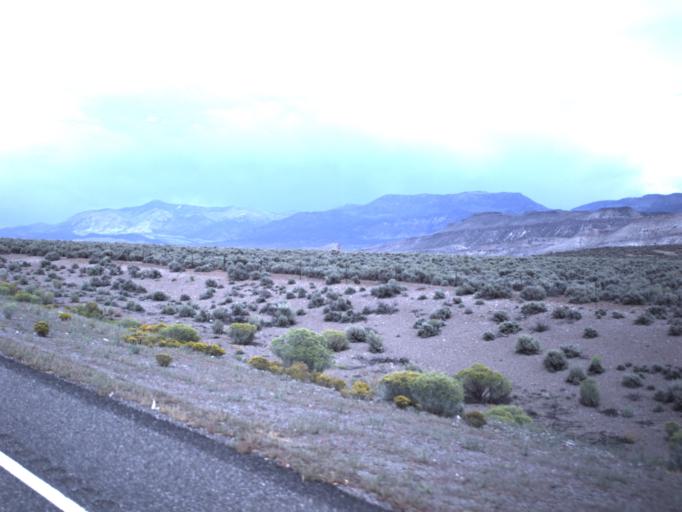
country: US
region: Utah
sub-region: Piute County
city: Junction
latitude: 38.2915
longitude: -112.2253
